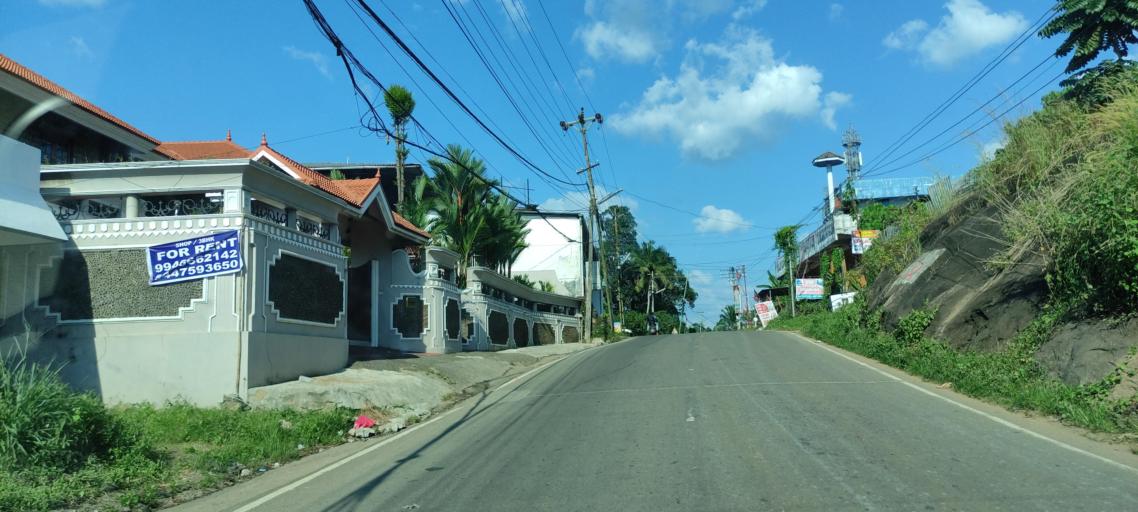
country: IN
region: Kerala
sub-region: Pattanamtitta
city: Pathanamthitta
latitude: 9.2672
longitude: 76.7944
